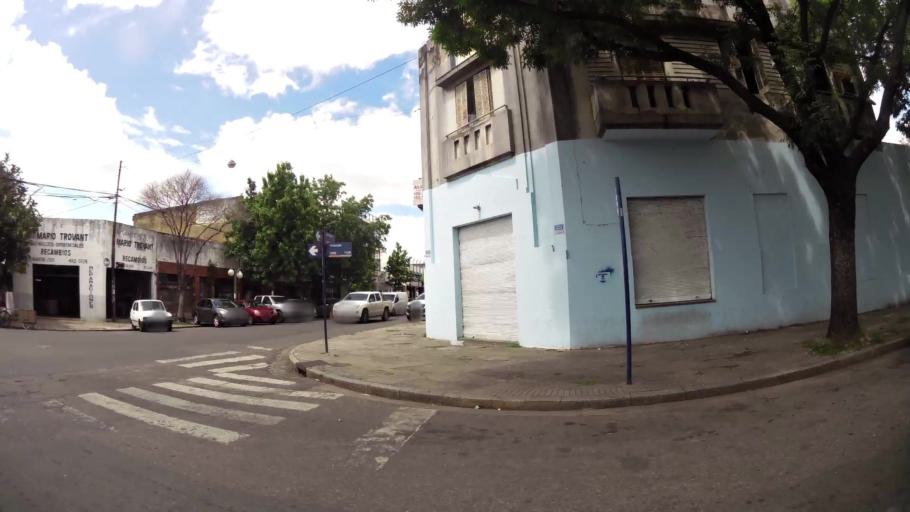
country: AR
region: Santa Fe
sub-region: Departamento de Rosario
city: Rosario
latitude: -32.9667
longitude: -60.6419
